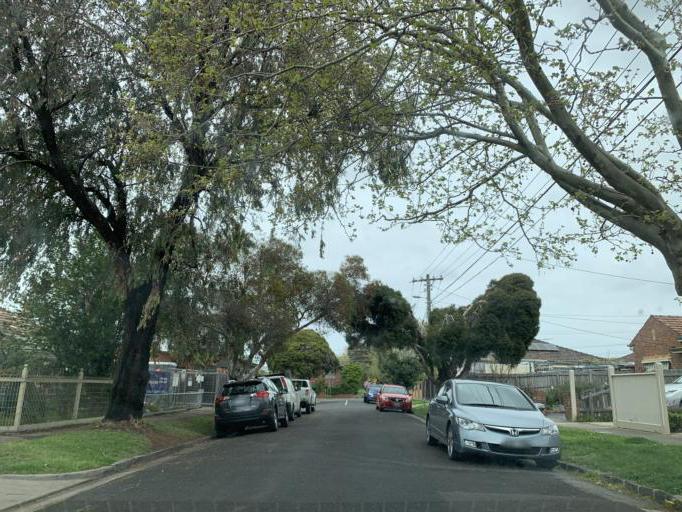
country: AU
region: Victoria
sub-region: Moreland
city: Pascoe Vale South
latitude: -37.7469
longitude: 144.9545
